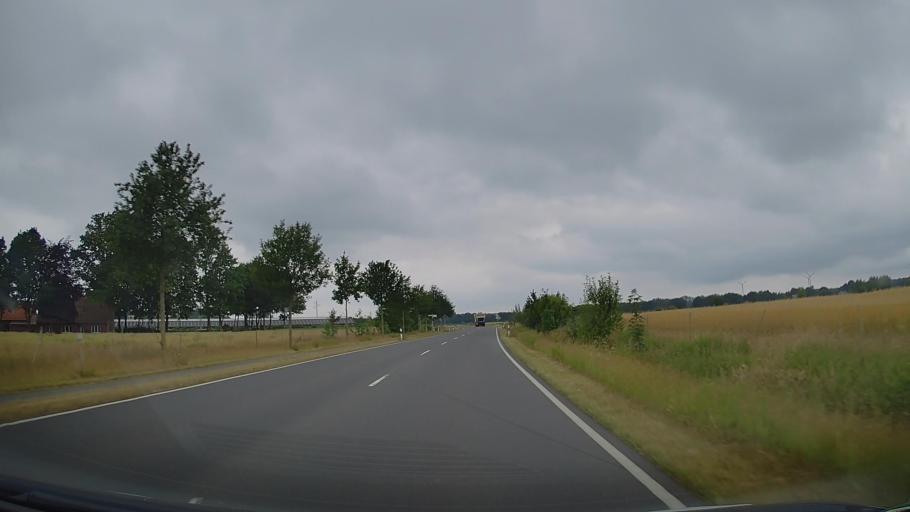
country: DE
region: Lower Saxony
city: Dinklage
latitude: 52.6794
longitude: 8.1163
